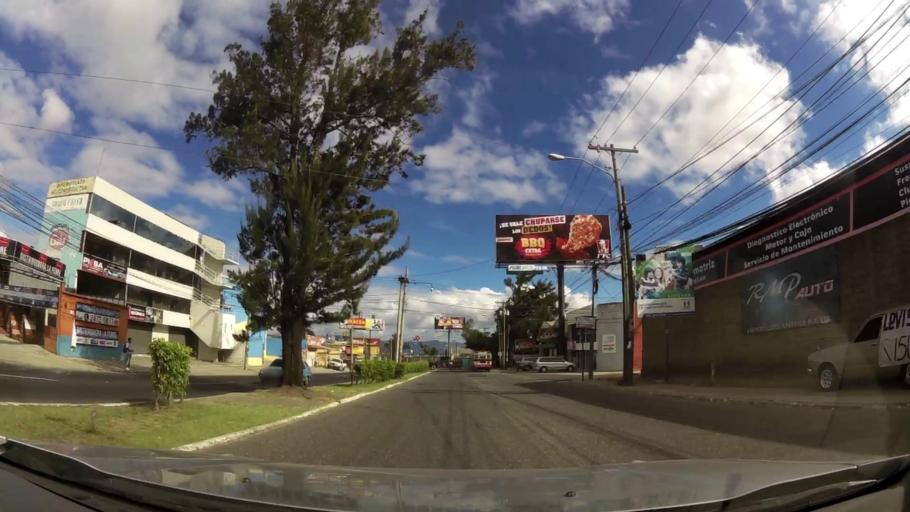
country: GT
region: Guatemala
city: Mixco
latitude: 14.6139
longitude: -90.6045
